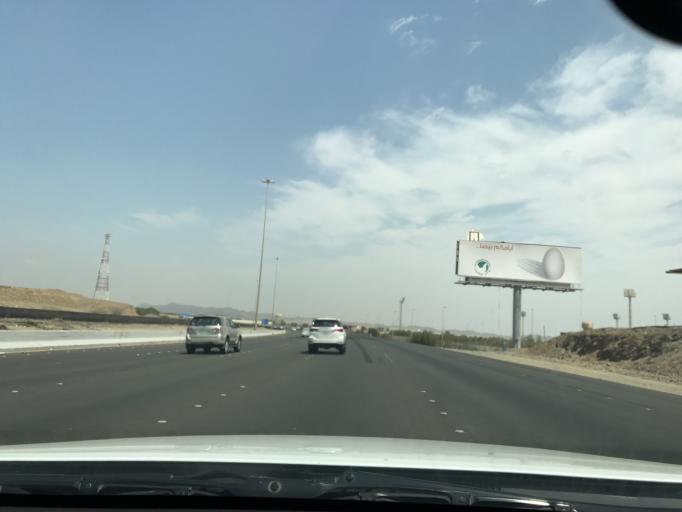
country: SA
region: Makkah
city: Jeddah
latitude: 21.3917
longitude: 39.4136
